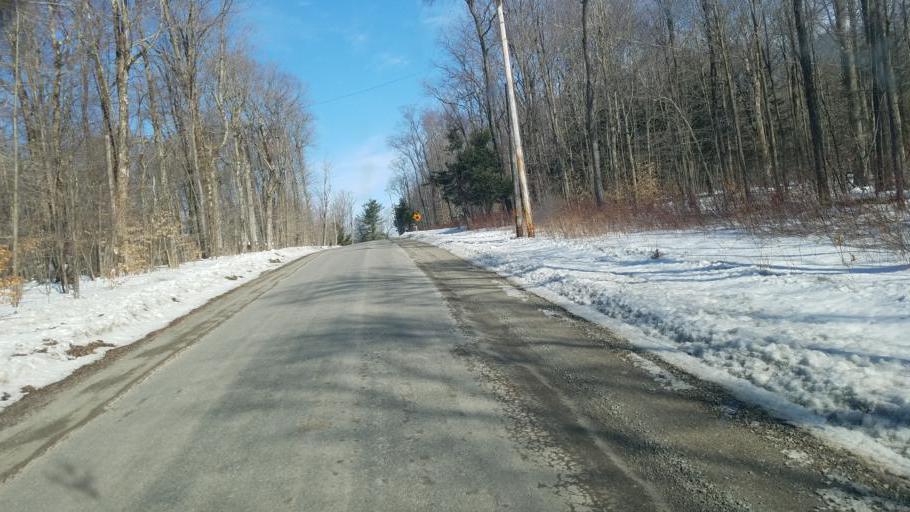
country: US
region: New York
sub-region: Allegany County
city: Andover
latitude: 42.0856
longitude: -77.7716
